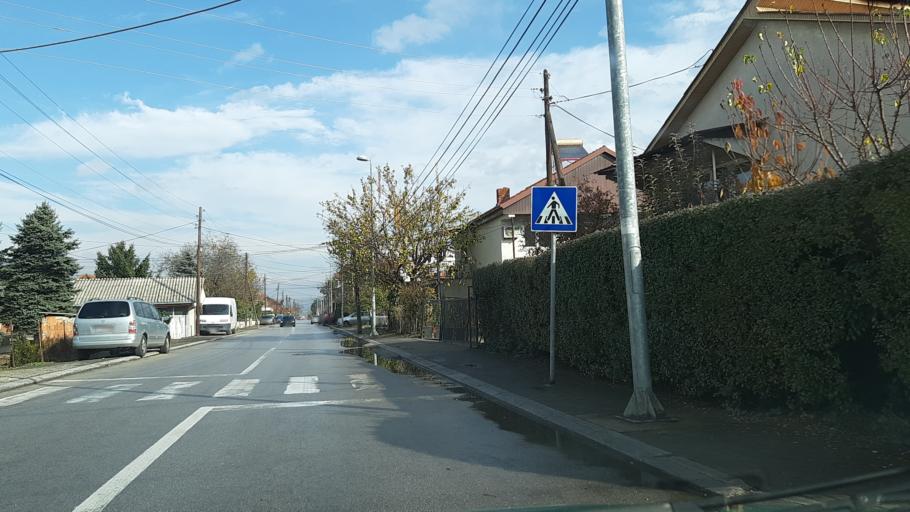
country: MK
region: Kisela Voda
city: Usje
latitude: 41.9781
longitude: 21.4851
